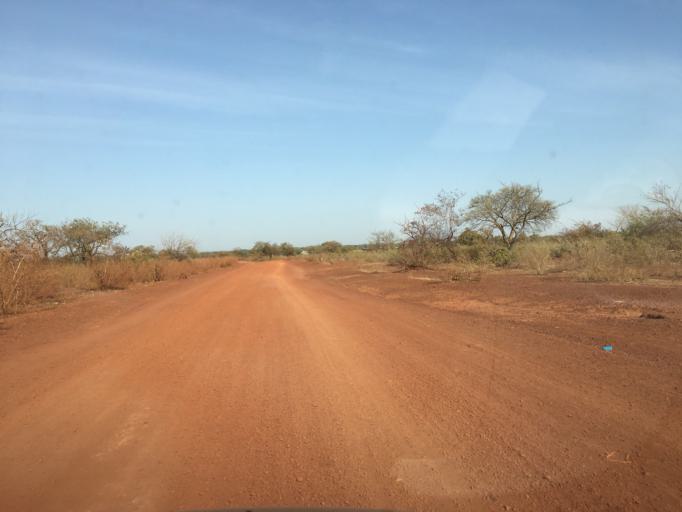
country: BF
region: Plateau-Central
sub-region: Province du Kourweogo
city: Bousse
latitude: 12.5626
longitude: -1.9032
